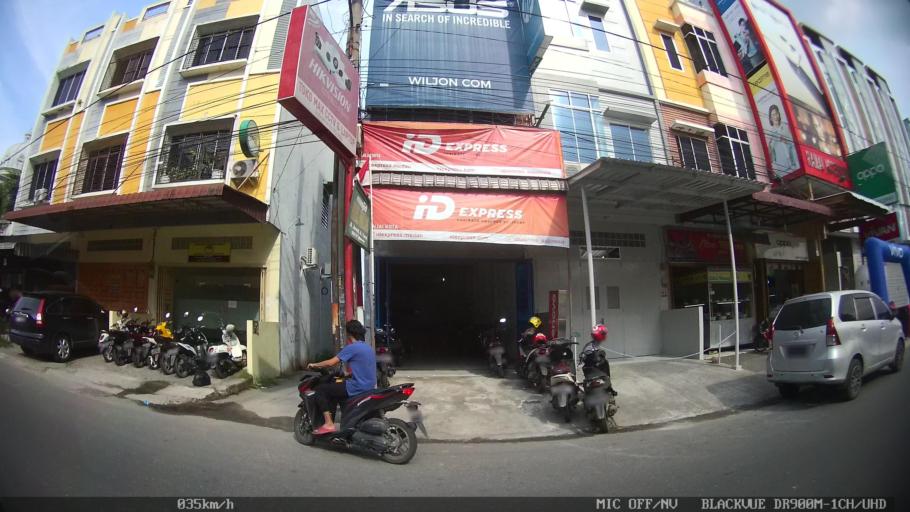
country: ID
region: North Sumatra
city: Binjai
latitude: 3.6019
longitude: 98.4863
